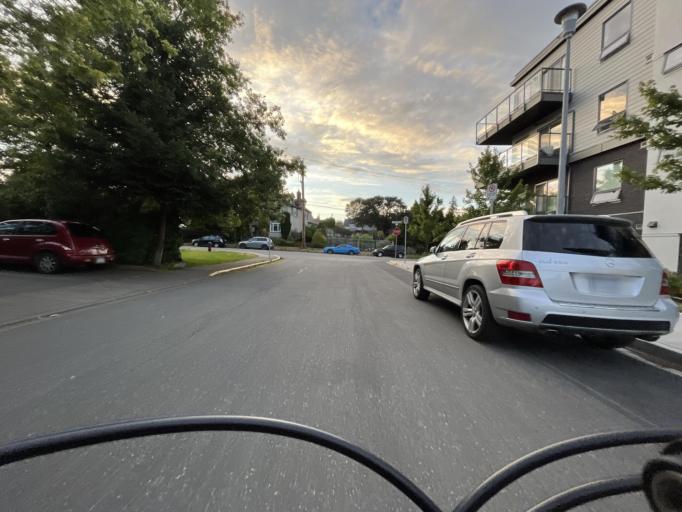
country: CA
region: British Columbia
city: Victoria
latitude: 48.4303
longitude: -123.3955
